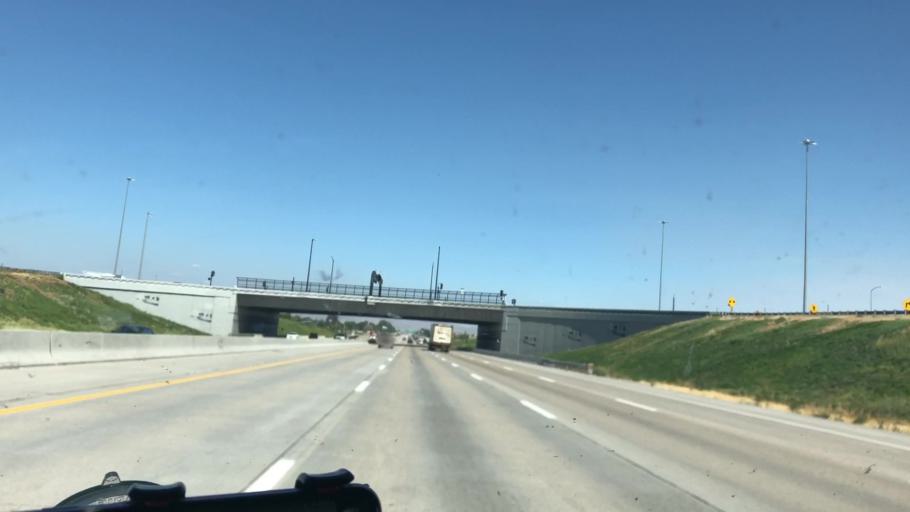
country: US
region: Idaho
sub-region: Ada County
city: Meridian
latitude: 43.5934
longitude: -116.4366
